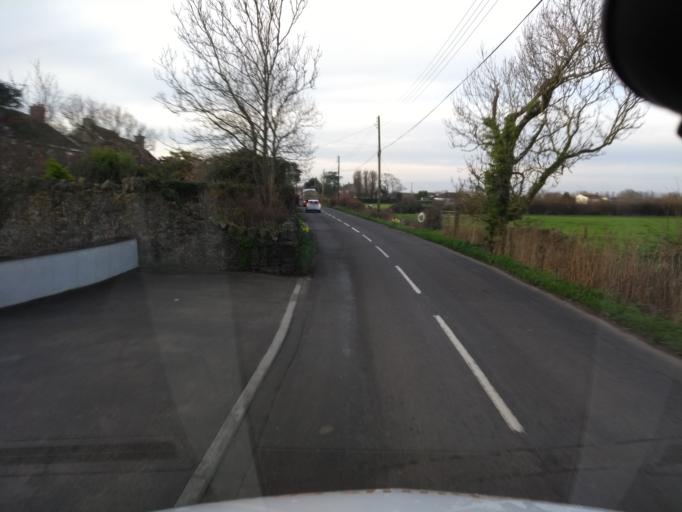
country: GB
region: England
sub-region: Somerset
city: Burnham-on-Sea
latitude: 51.2621
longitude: -2.9617
